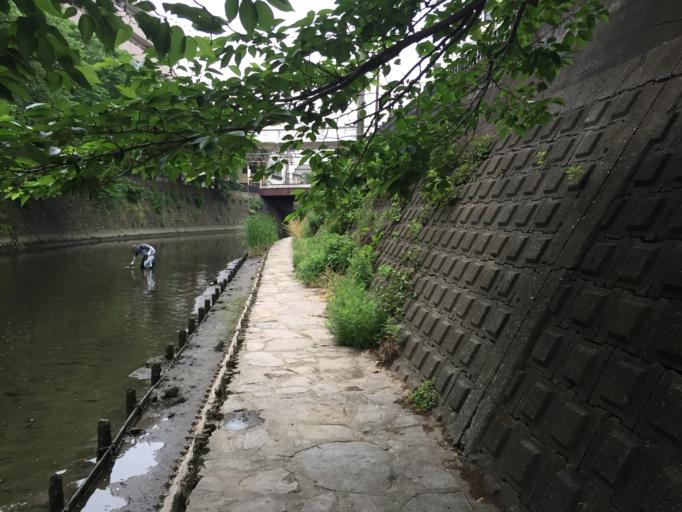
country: JP
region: Kanagawa
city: Yokohama
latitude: 35.4241
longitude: 139.6002
